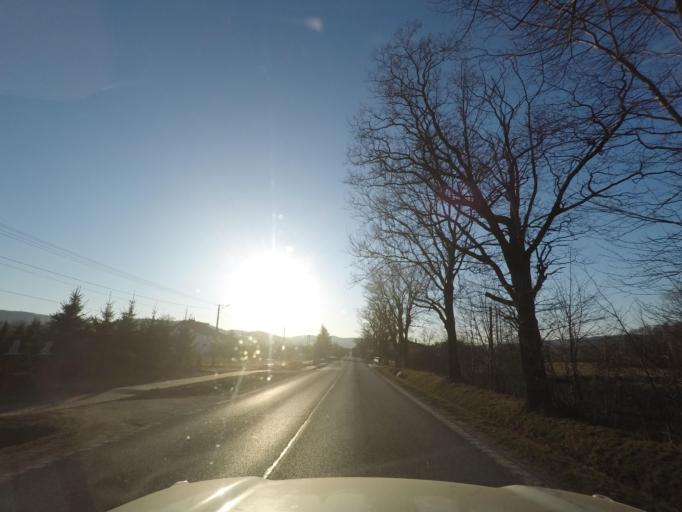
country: PL
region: Subcarpathian Voivodeship
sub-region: Powiat krosnienski
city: Dukla
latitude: 49.5579
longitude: 21.6374
